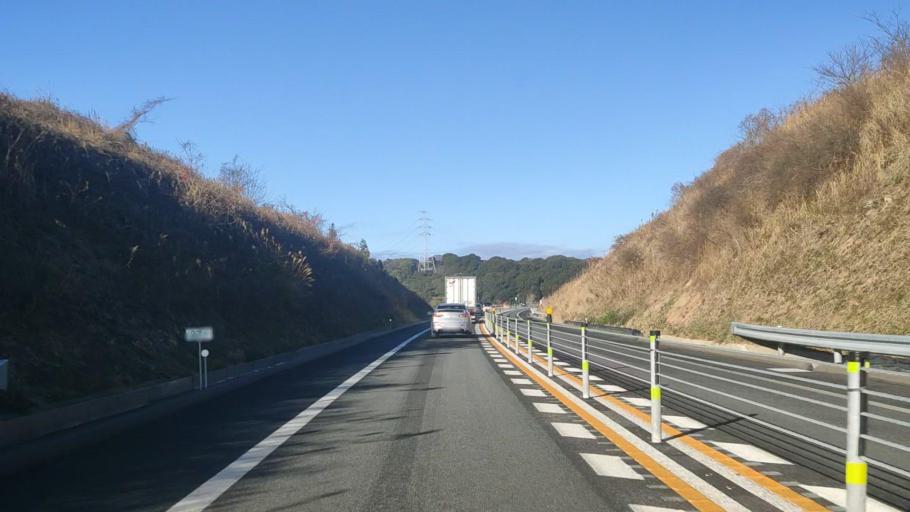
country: JP
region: Fukuoka
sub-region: Buzen-shi
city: Buzen
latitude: 33.6015
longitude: 131.1051
